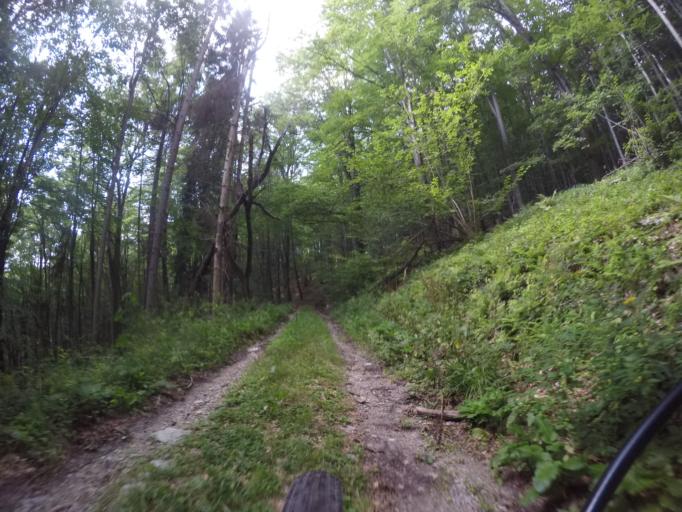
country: SK
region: Kosicky
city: Gelnica
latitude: 48.9219
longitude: 21.0165
